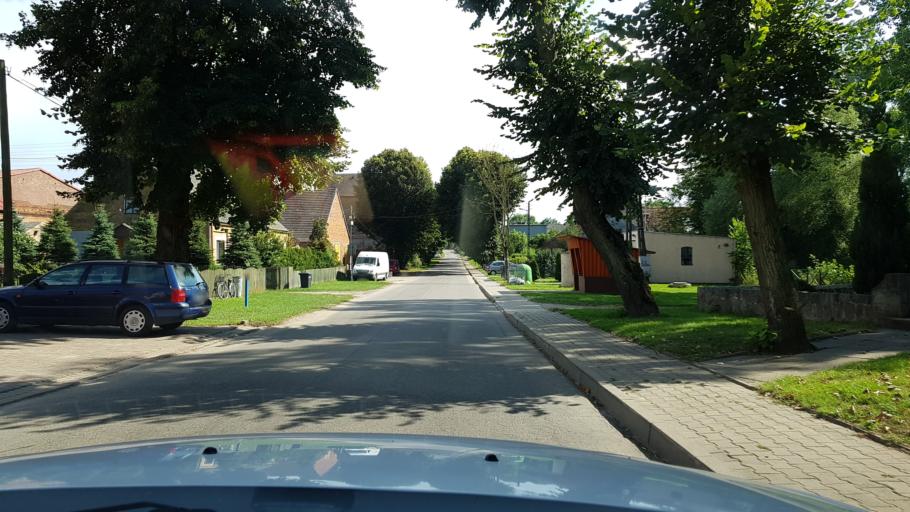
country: PL
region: West Pomeranian Voivodeship
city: Trzcinsko Zdroj
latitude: 52.9532
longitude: 14.5491
